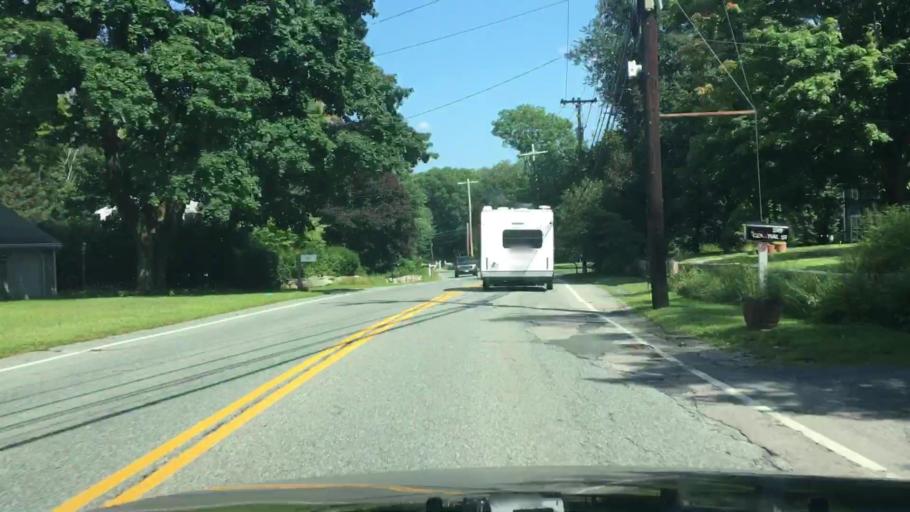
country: US
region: Massachusetts
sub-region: Middlesex County
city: Holliston
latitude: 42.2011
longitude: -71.4195
